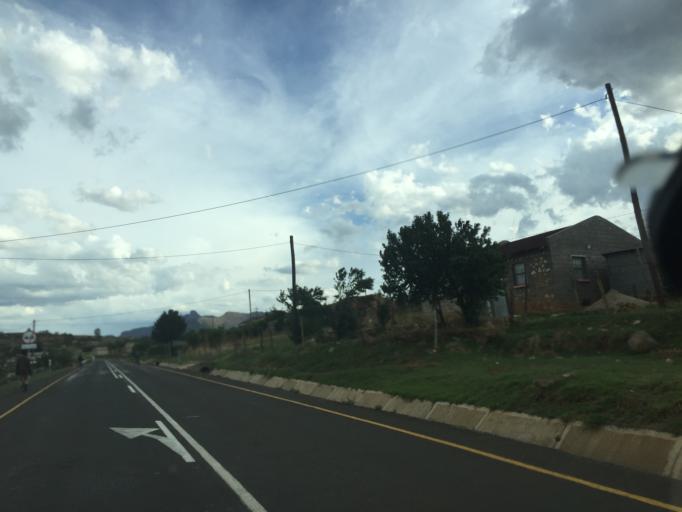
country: LS
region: Berea
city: Teyateyaneng
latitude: -29.1320
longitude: 27.9865
